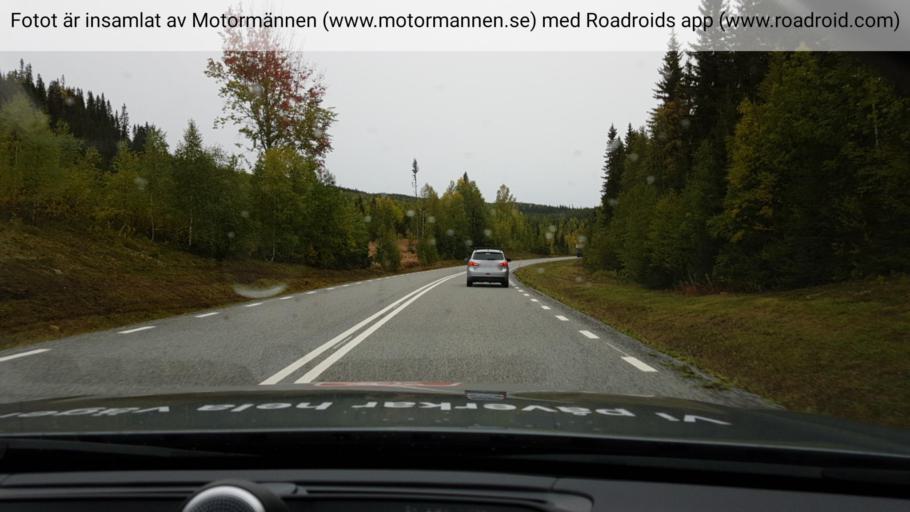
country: SE
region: Jaemtland
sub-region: Stroemsunds Kommun
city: Stroemsund
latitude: 64.0760
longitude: 15.5610
